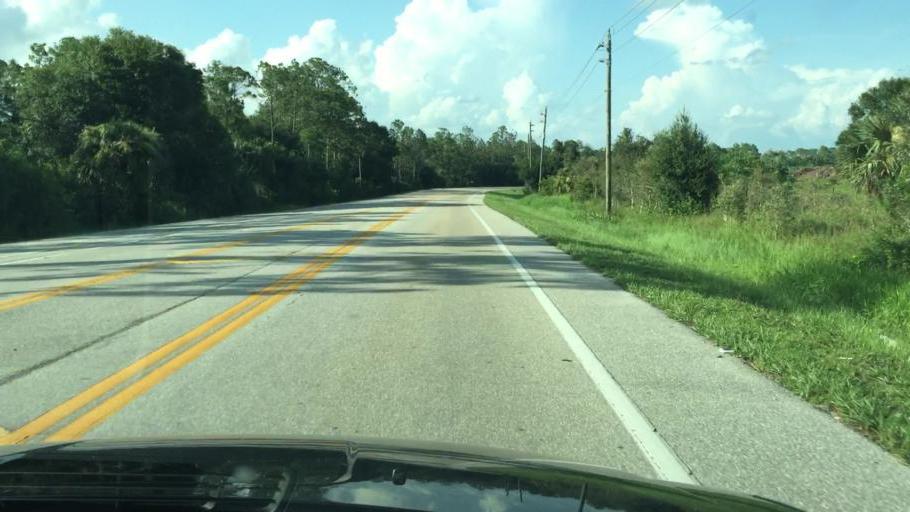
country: US
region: Florida
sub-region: Lee County
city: Buckingham
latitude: 26.6320
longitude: -81.7560
